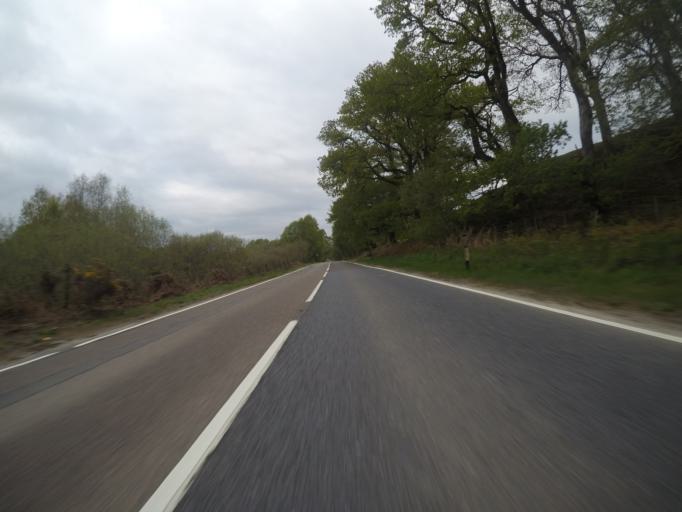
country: GB
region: Scotland
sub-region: Highland
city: Spean Bridge
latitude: 56.8946
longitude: -4.8925
